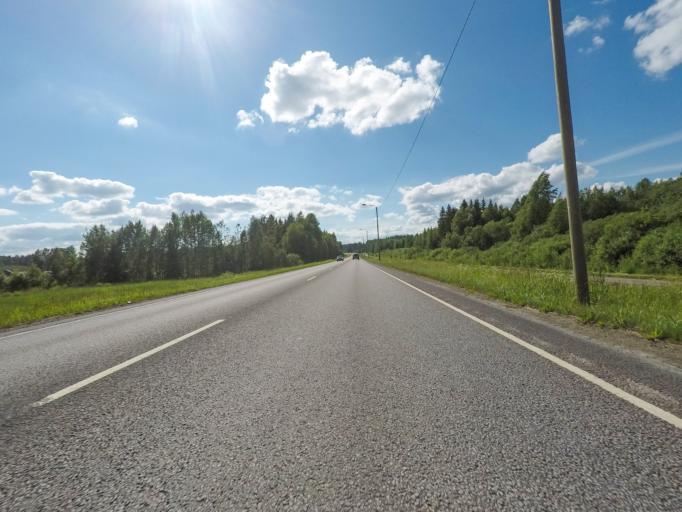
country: FI
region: Southern Savonia
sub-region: Savonlinna
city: Savonlinna
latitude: 61.8803
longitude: 29.0299
